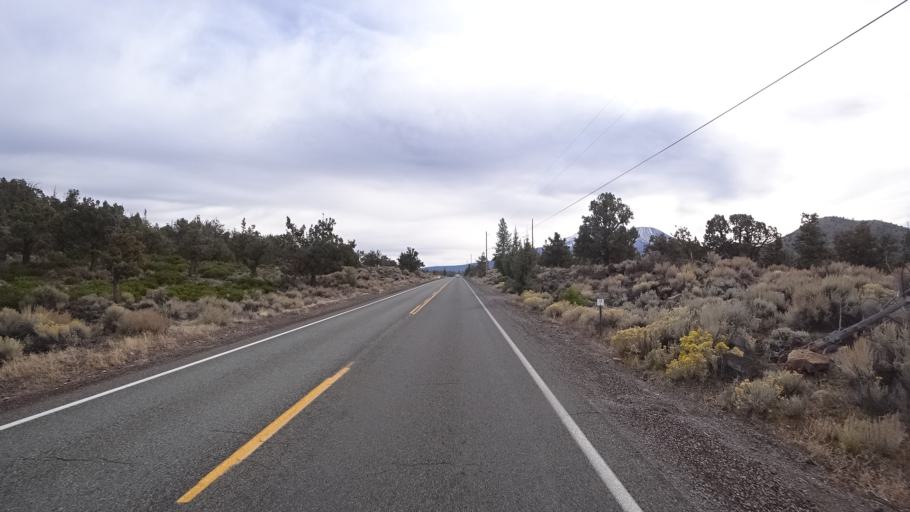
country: US
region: California
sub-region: Siskiyou County
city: Weed
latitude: 41.5596
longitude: -122.2586
